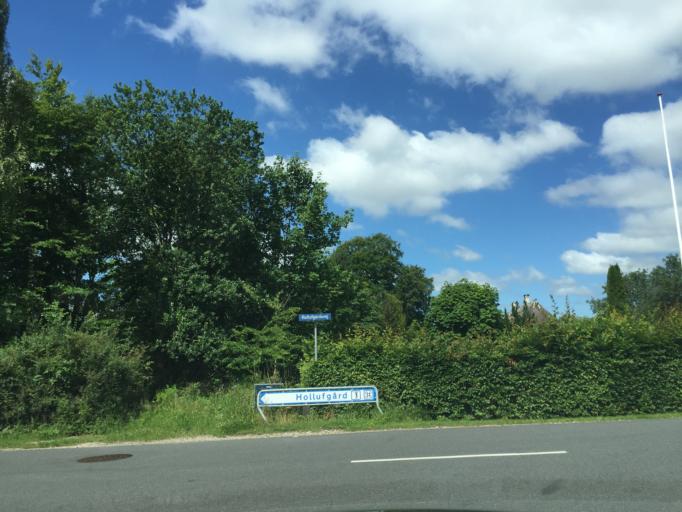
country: DK
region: South Denmark
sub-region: Odense Kommune
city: Neder Holluf
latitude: 55.3586
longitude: 10.4460
